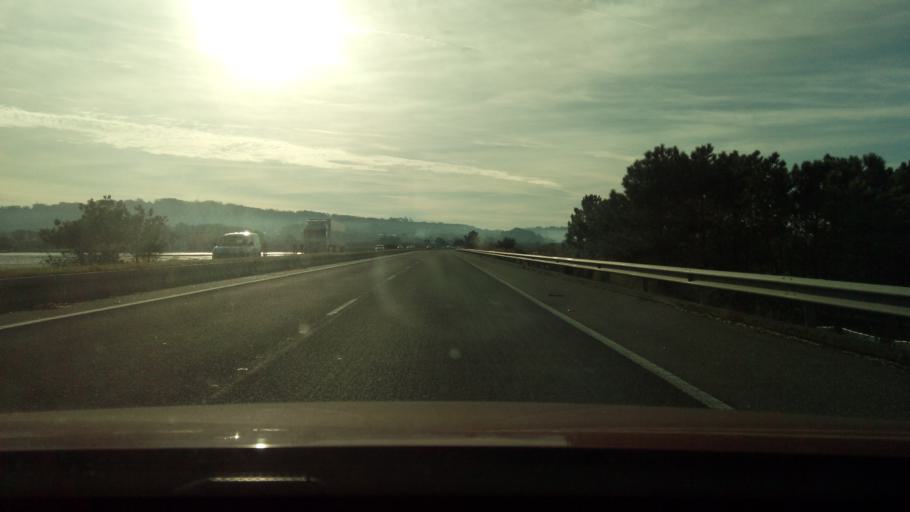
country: ES
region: Galicia
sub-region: Provincia de Pontevedra
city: O Grove
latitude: 42.4530
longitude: -8.8725
